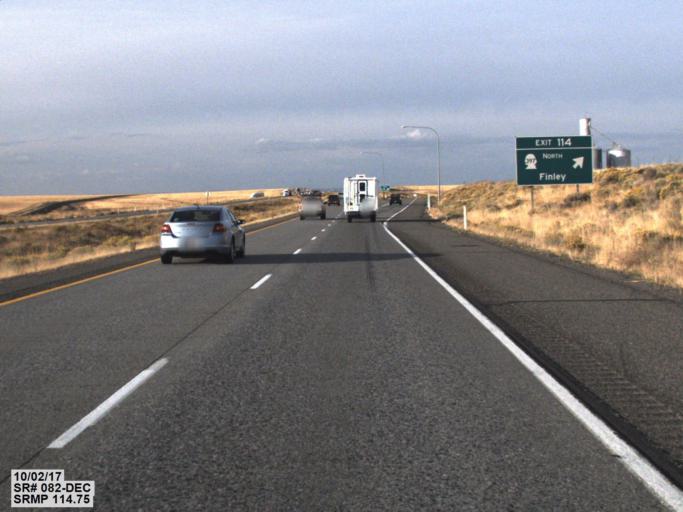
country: US
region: Washington
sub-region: Benton County
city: Highland
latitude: 46.1373
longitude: -119.2019
